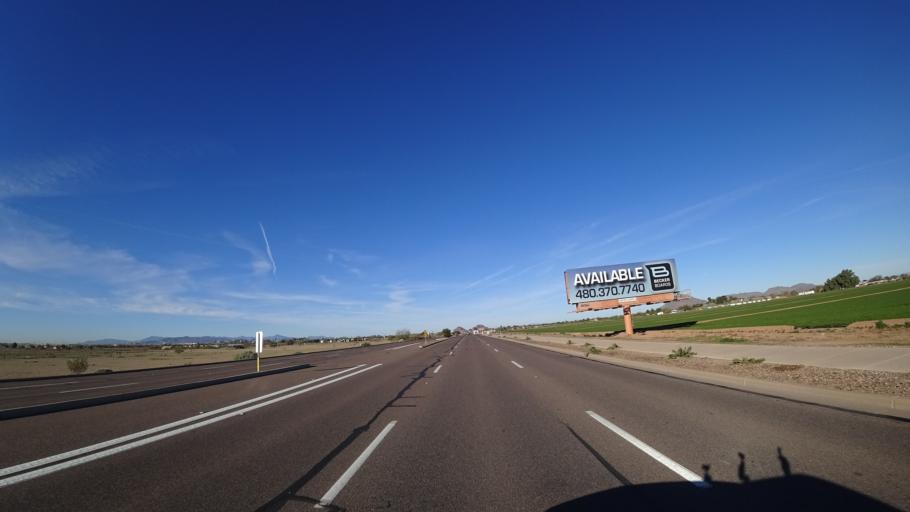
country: US
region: Arizona
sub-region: Maricopa County
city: Scottsdale
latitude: 33.4659
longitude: -111.8693
